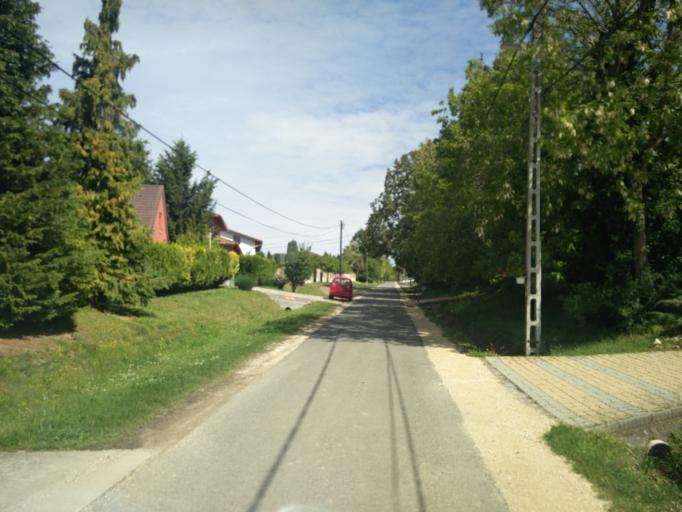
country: HU
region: Tolna
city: Szentgalpuszta
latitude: 46.2794
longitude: 18.6370
